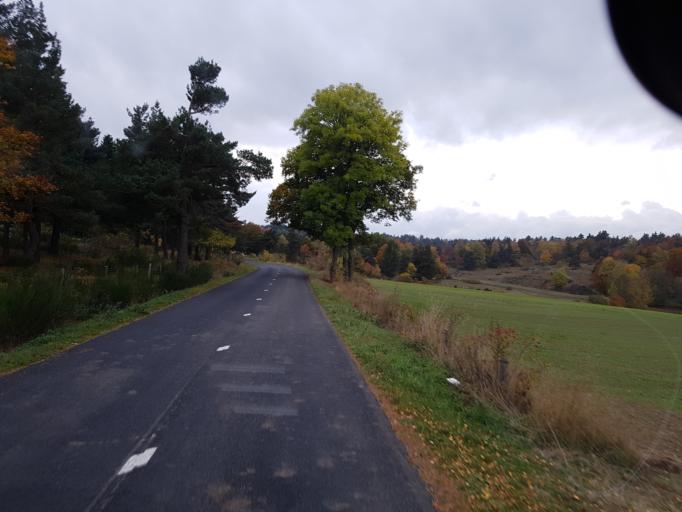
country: FR
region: Languedoc-Roussillon
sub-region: Departement de la Lozere
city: Langogne
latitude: 44.7236
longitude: 3.7683
